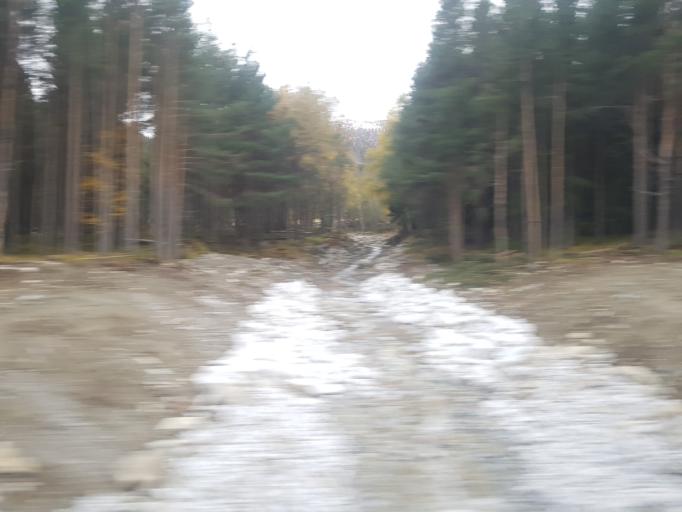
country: NO
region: Oppland
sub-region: Dovre
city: Dovre
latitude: 61.9232
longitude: 9.3365
